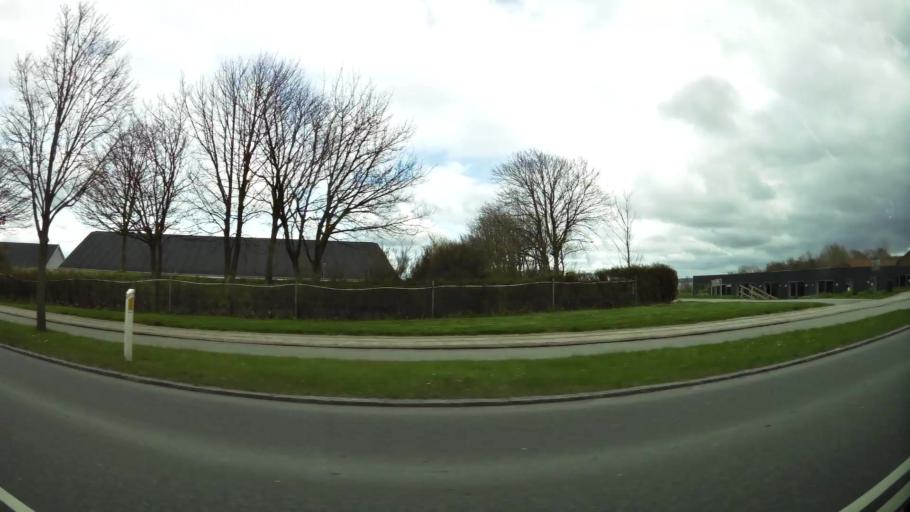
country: DK
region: North Denmark
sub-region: Thisted Kommune
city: Thisted
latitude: 56.9466
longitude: 8.6600
